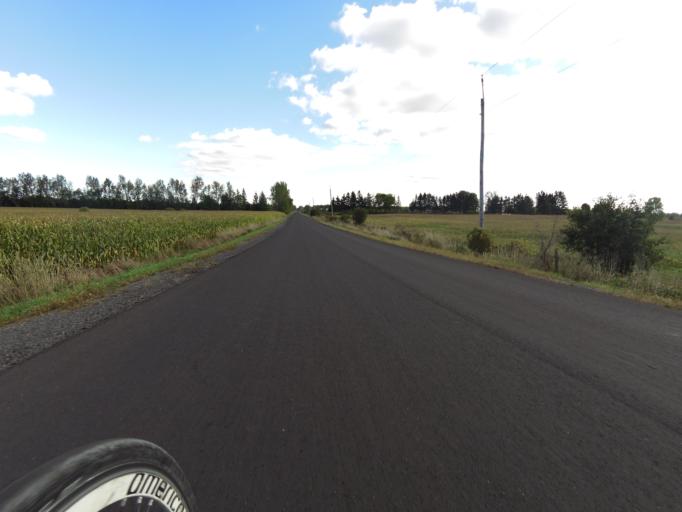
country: CA
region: Ontario
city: Bells Corners
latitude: 45.1166
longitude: -75.6636
